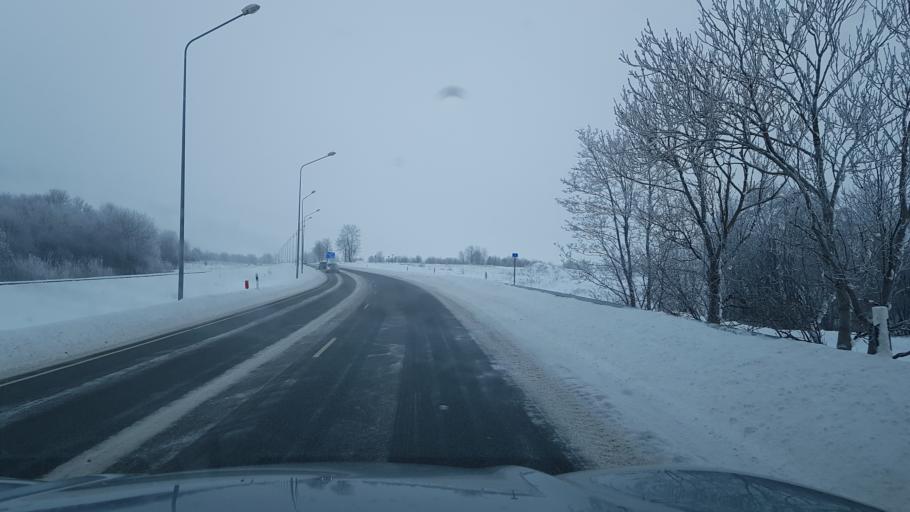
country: EE
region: Ida-Virumaa
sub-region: Johvi vald
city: Johvi
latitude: 59.3443
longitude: 27.4044
